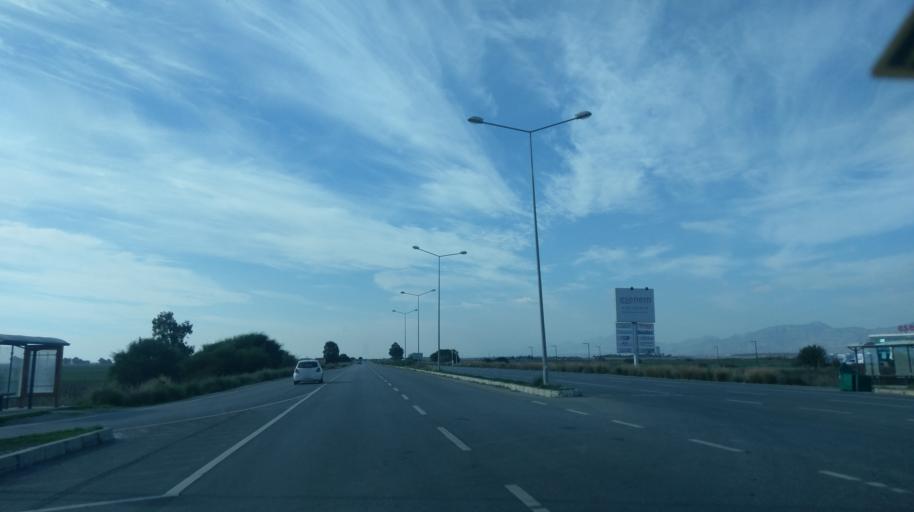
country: CY
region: Ammochostos
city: Lefkonoiko
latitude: 35.1870
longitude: 33.6400
